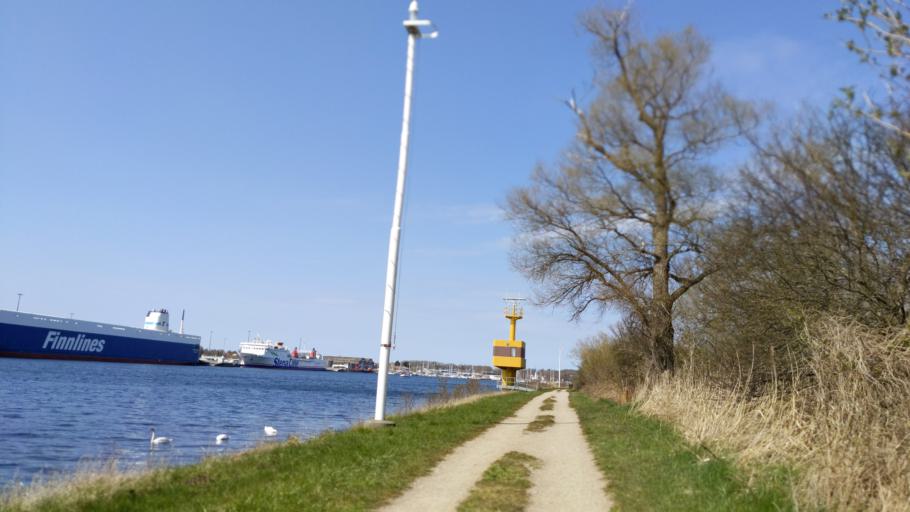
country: DE
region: Schleswig-Holstein
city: Travemuende
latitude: 53.9447
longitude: 10.8638
